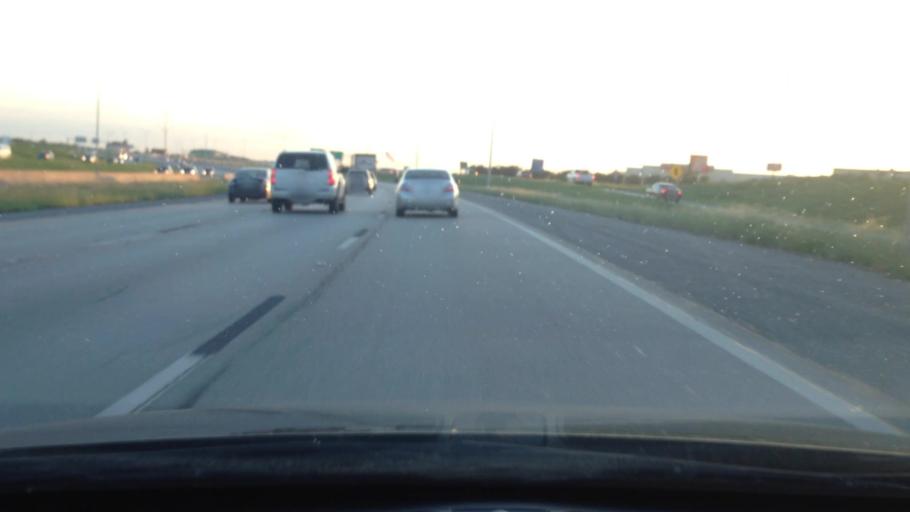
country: US
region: Texas
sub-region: Tarrant County
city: Sansom Park
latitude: 32.8137
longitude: -97.4135
